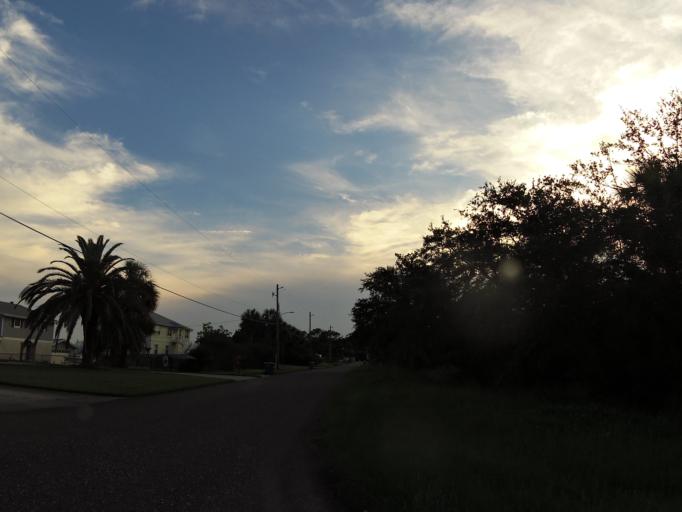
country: US
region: Florida
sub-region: Duval County
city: Atlantic Beach
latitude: 30.3945
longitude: -81.4931
